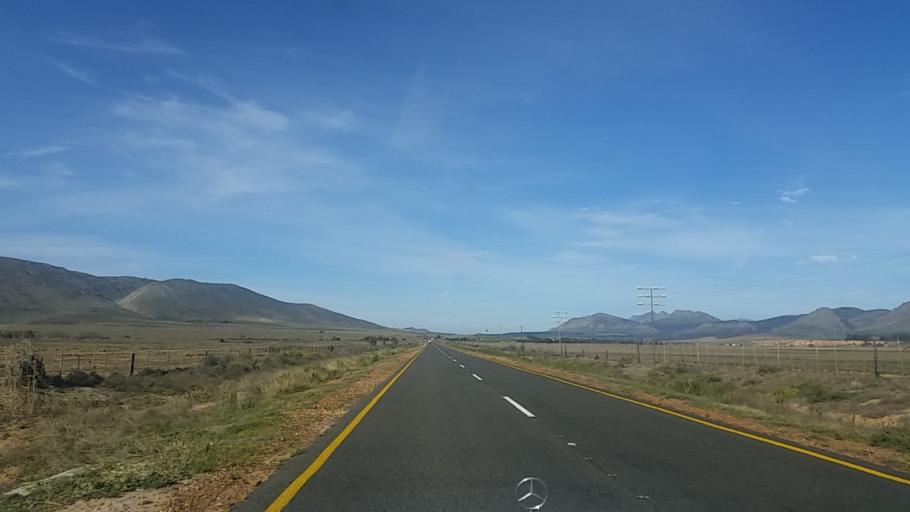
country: ZA
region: Western Cape
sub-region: Eden District Municipality
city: George
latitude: -33.8092
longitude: 22.5474
